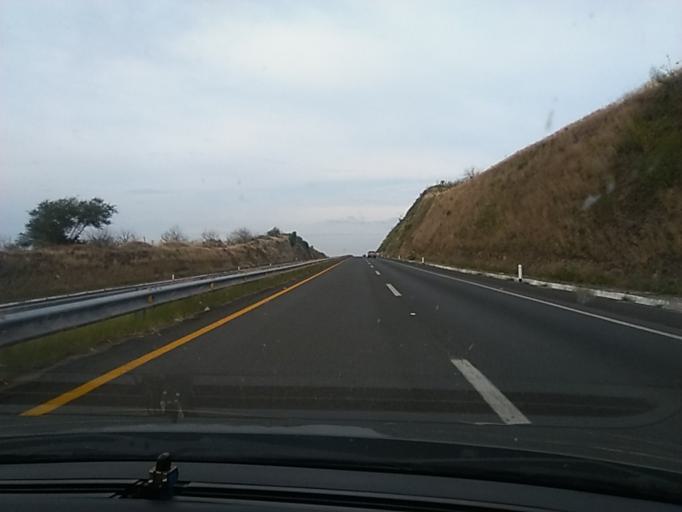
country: MX
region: Michoacan
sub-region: Zinapecuaro
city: Francisco Villa
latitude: 19.8825
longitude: -100.9268
